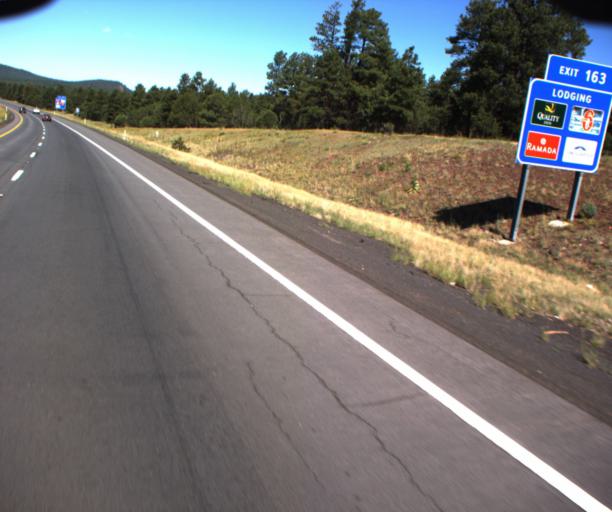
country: US
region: Arizona
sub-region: Coconino County
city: Williams
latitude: 35.2638
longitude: -112.1602
